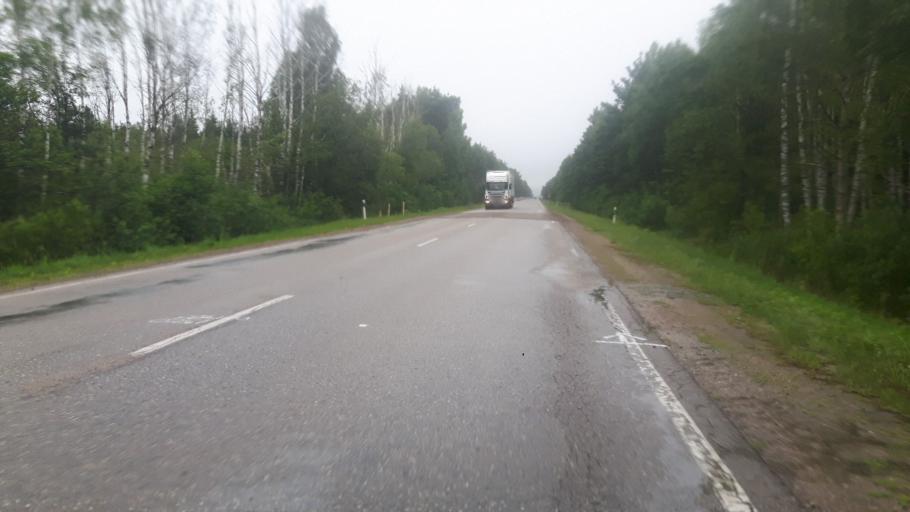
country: LV
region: Rucavas
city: Rucava
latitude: 56.1415
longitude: 21.1519
